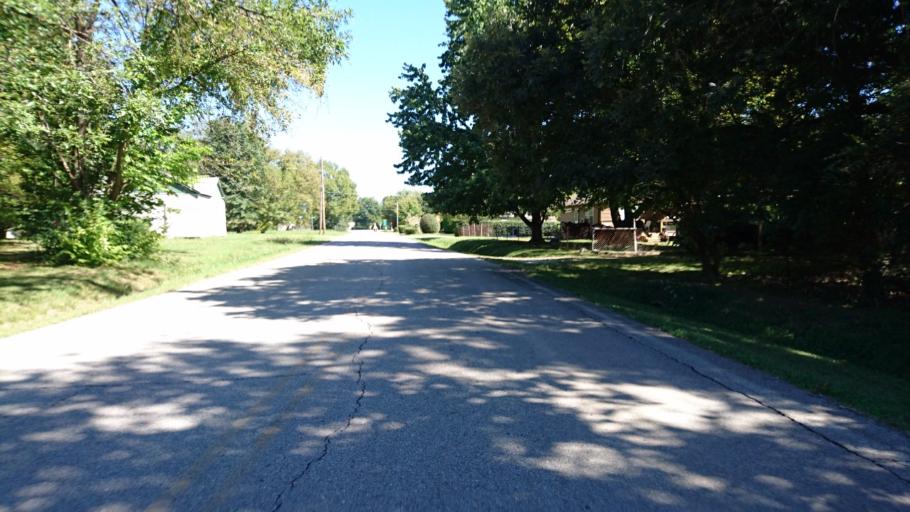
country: US
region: Kansas
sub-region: Cherokee County
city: Baxter Springs
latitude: 37.0332
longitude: -94.7377
